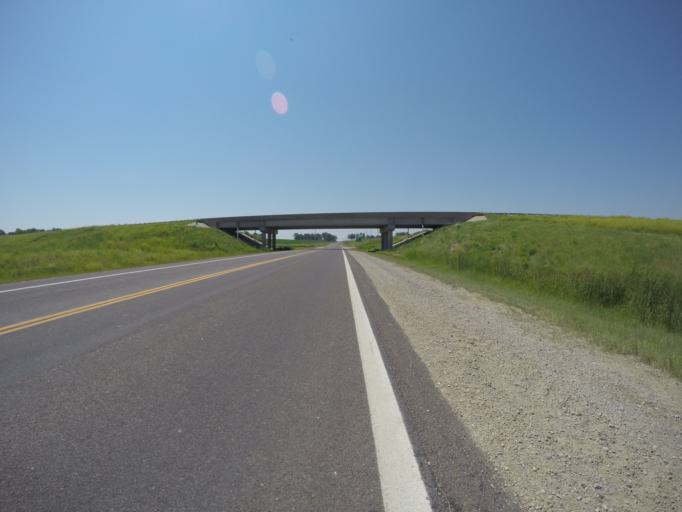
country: US
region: Kansas
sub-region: Doniphan County
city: Highland
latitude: 39.8405
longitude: -95.2652
